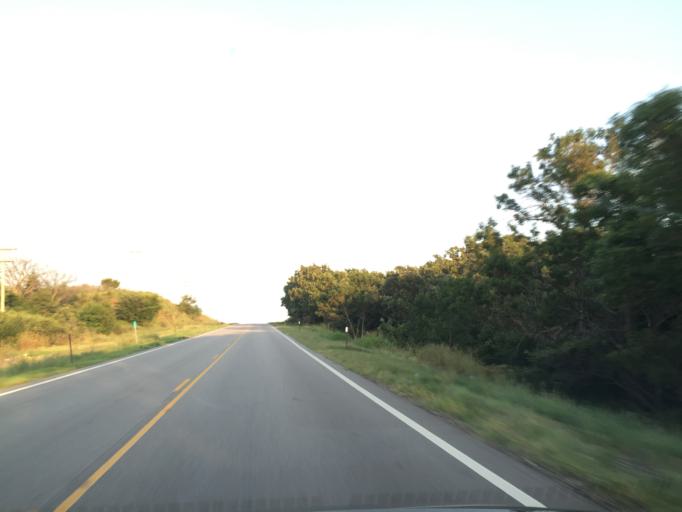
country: US
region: Kansas
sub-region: Ellsworth County
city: Ellsworth
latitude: 38.7001
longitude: -98.2159
